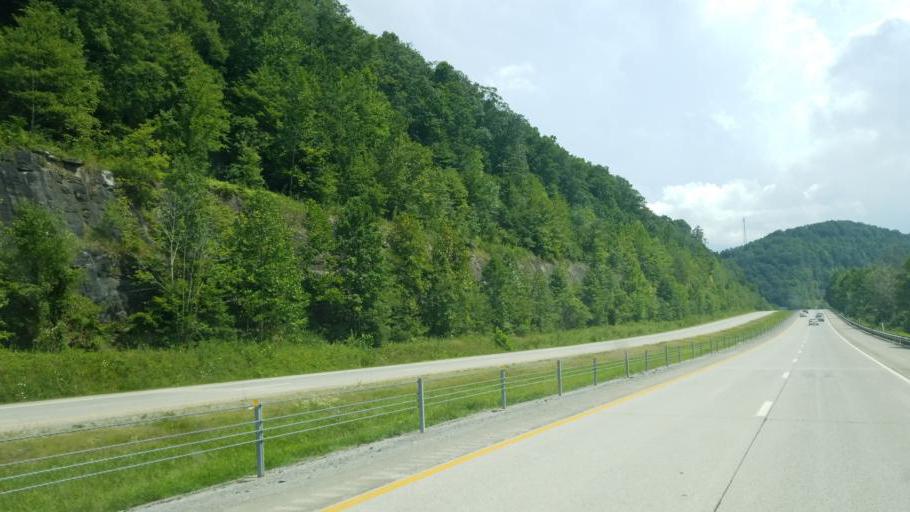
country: US
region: West Virginia
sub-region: Boone County
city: Madison
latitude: 38.1724
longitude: -81.8502
